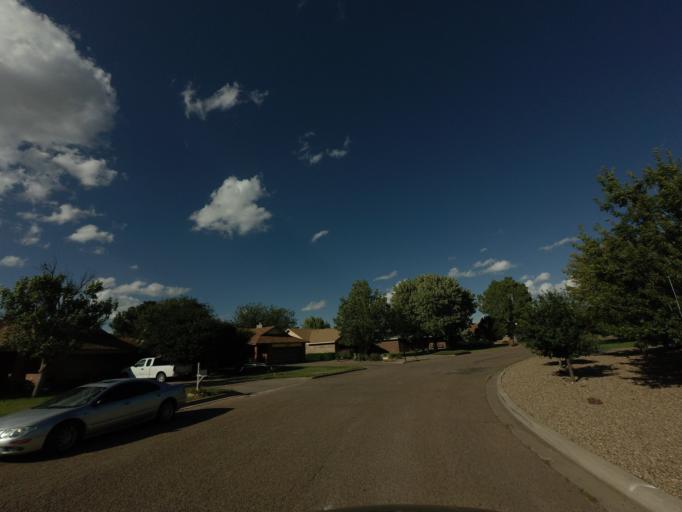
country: US
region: New Mexico
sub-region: Curry County
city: Clovis
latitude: 34.4341
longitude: -103.1812
